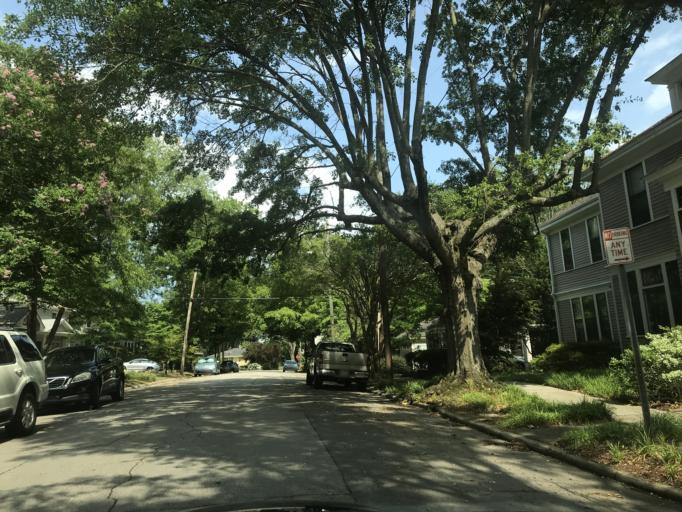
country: US
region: North Carolina
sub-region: Wake County
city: Raleigh
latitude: 35.7757
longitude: -78.6521
